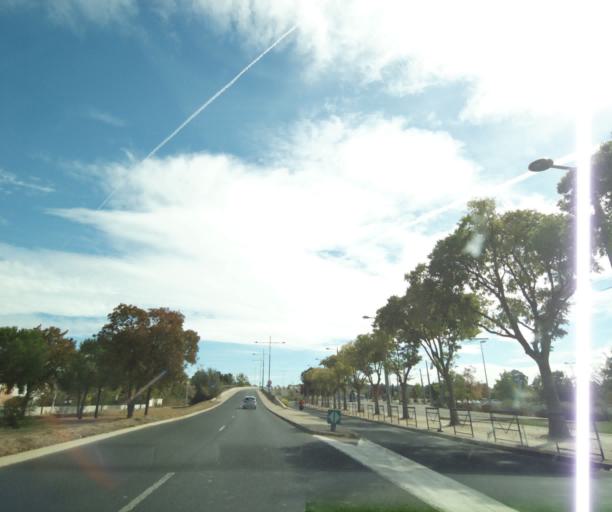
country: FR
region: Languedoc-Roussillon
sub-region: Departement de l'Herault
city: Juvignac
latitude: 43.6184
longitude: 3.8183
